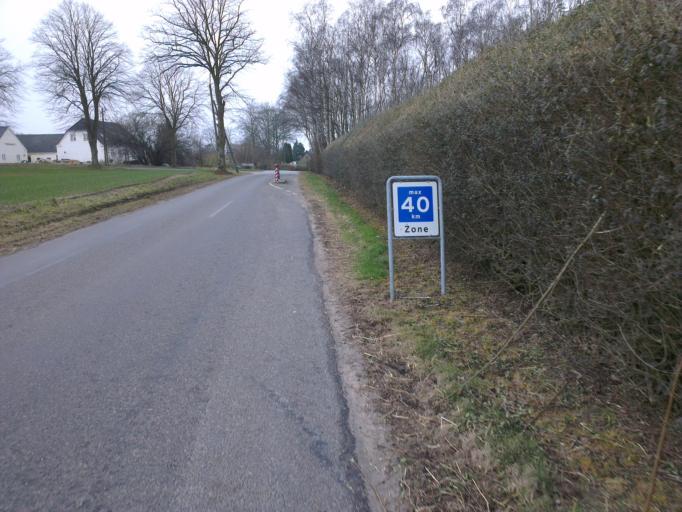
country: DK
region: Capital Region
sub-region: Frederikssund Kommune
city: Skibby
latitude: 55.7932
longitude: 11.9615
